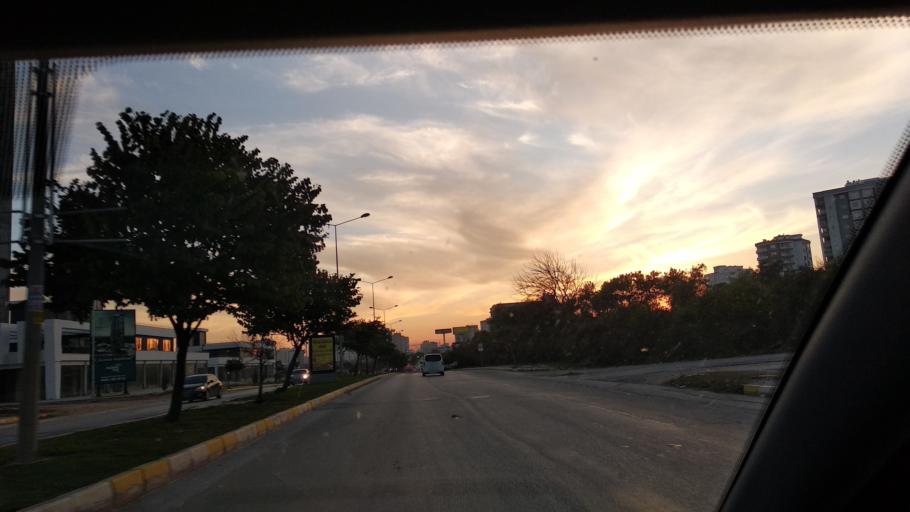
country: TR
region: Mersin
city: Mercin
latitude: 36.7993
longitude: 34.5805
